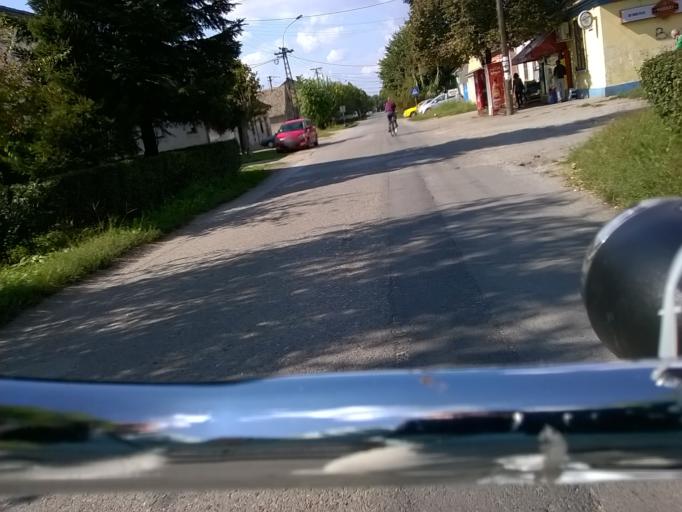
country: RS
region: Autonomna Pokrajina Vojvodina
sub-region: Juznobanatski Okrug
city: Pancevo
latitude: 44.8762
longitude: 20.6386
